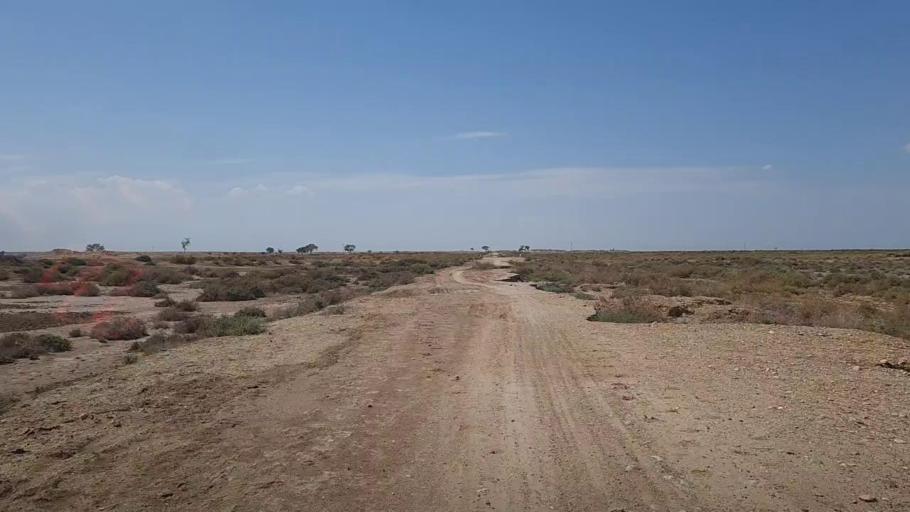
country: PK
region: Sindh
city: Sehwan
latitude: 26.3561
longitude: 67.6706
